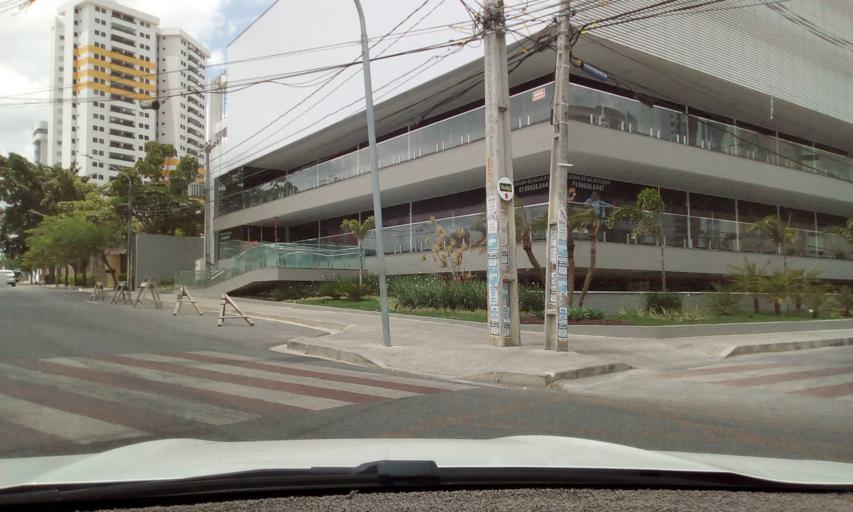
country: BR
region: Pernambuco
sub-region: Caruaru
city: Caruaru
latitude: -8.2700
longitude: -35.9758
